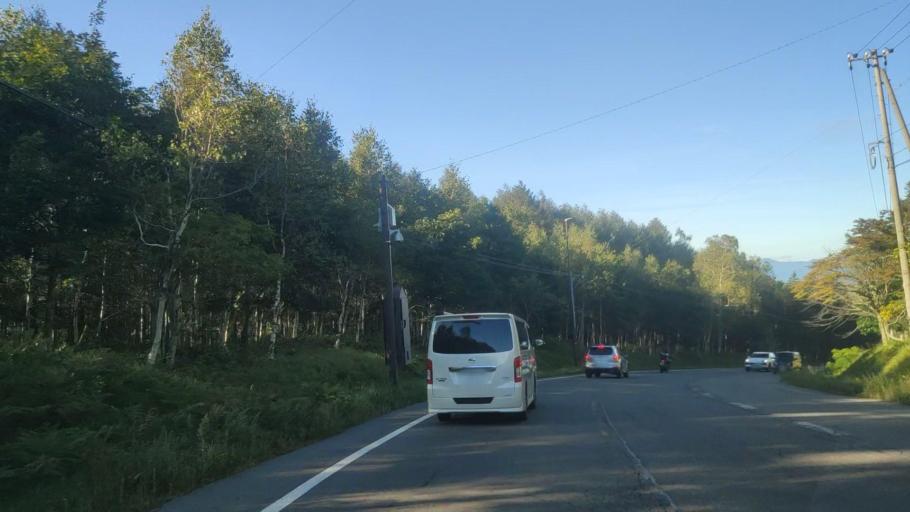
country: JP
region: Nagano
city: Kamimaruko
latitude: 36.1596
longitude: 138.2793
